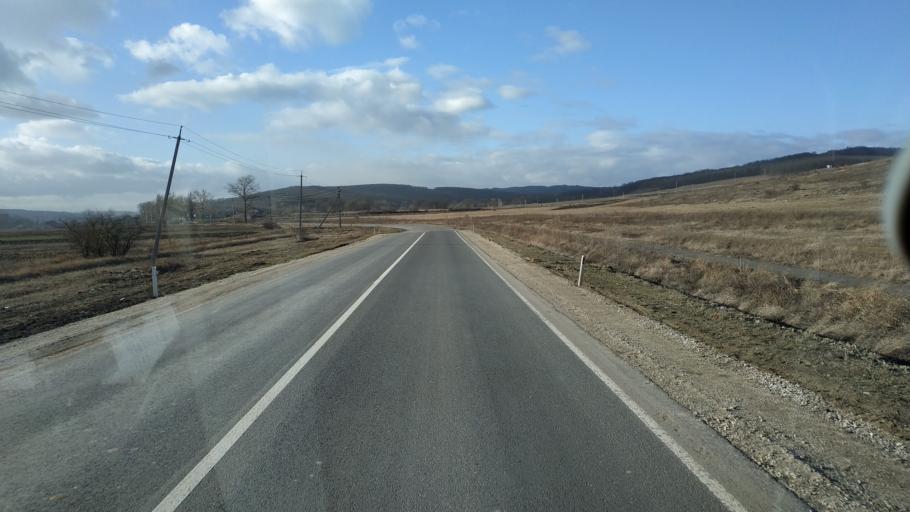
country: MD
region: Calarasi
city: Calarasi
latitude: 47.3260
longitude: 28.1018
